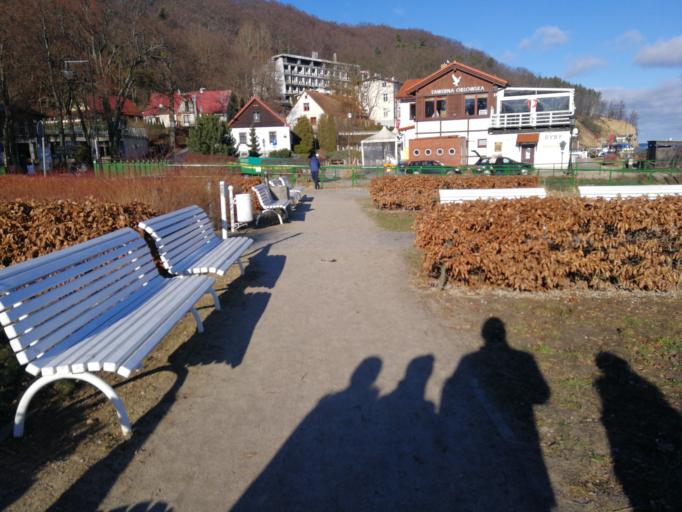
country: PL
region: Pomeranian Voivodeship
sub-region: Sopot
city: Sopot
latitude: 54.4807
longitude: 18.5642
